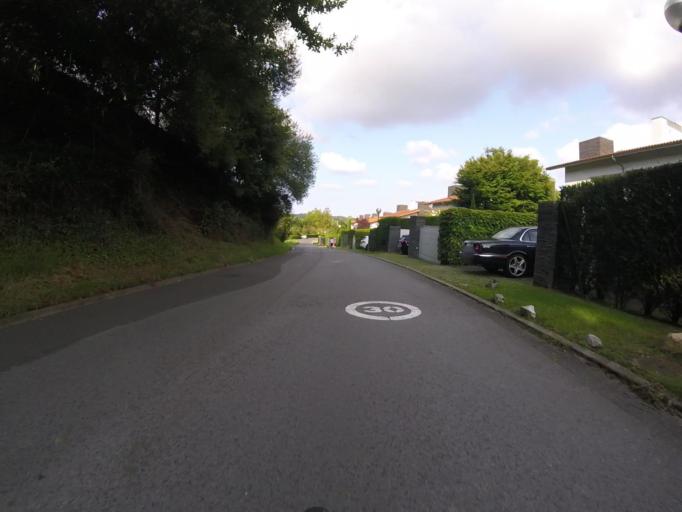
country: ES
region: Basque Country
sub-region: Provincia de Guipuzcoa
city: Irun
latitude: 43.3417
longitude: -1.8216
